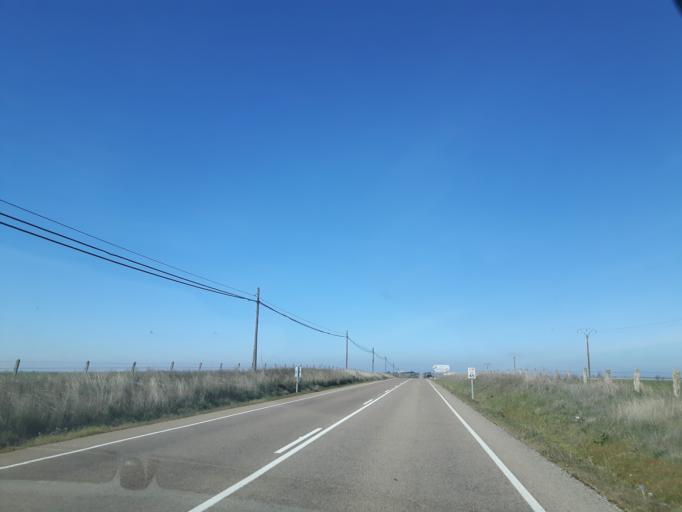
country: ES
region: Castille and Leon
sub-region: Provincia de Salamanca
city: Vitigudino
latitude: 41.0106
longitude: -6.4543
